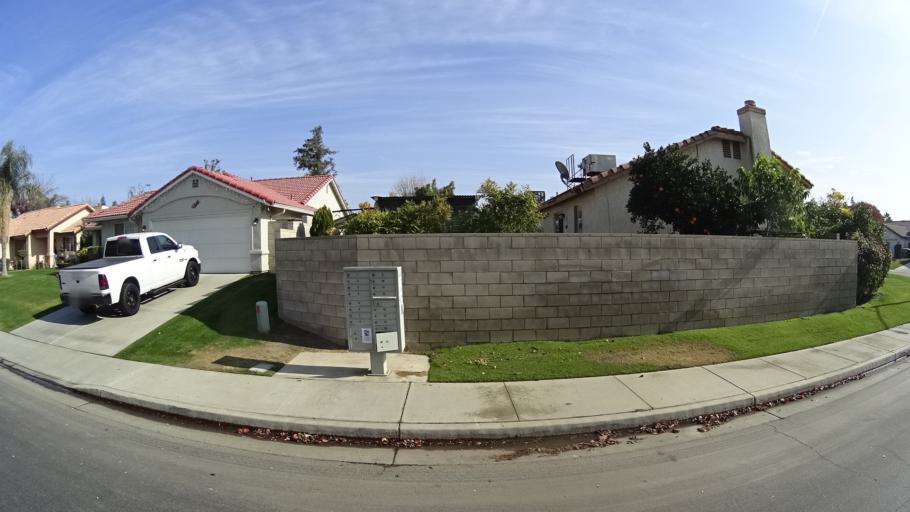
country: US
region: California
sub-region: Kern County
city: Greenacres
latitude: 35.3664
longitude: -119.1039
